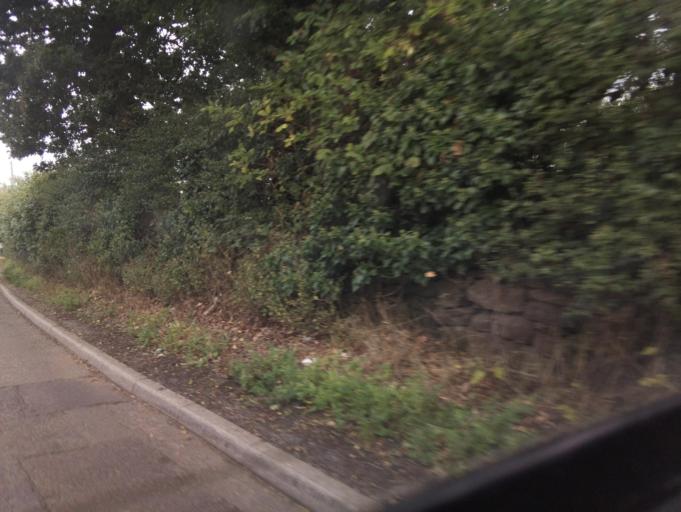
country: GB
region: England
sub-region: Telford and Wrekin
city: Newport
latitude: 52.7948
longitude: -2.3523
